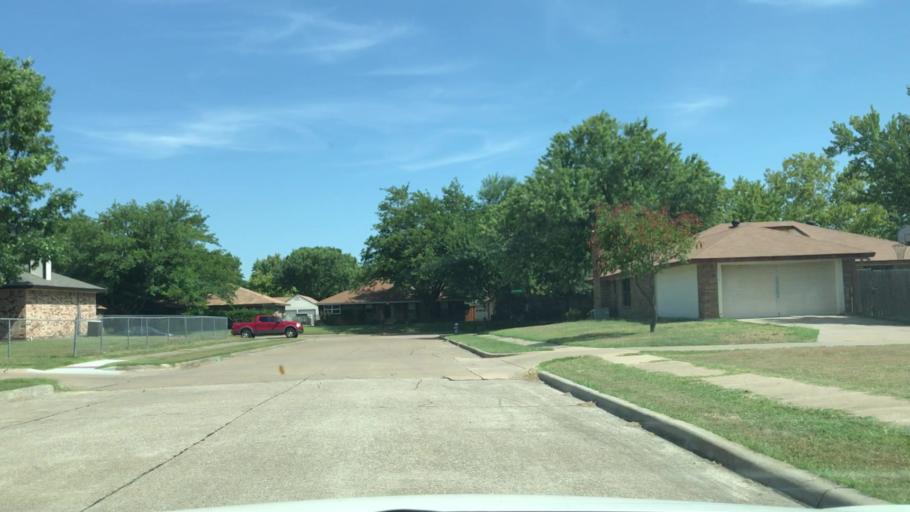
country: US
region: Texas
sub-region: Dallas County
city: Garland
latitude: 32.9337
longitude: -96.6167
